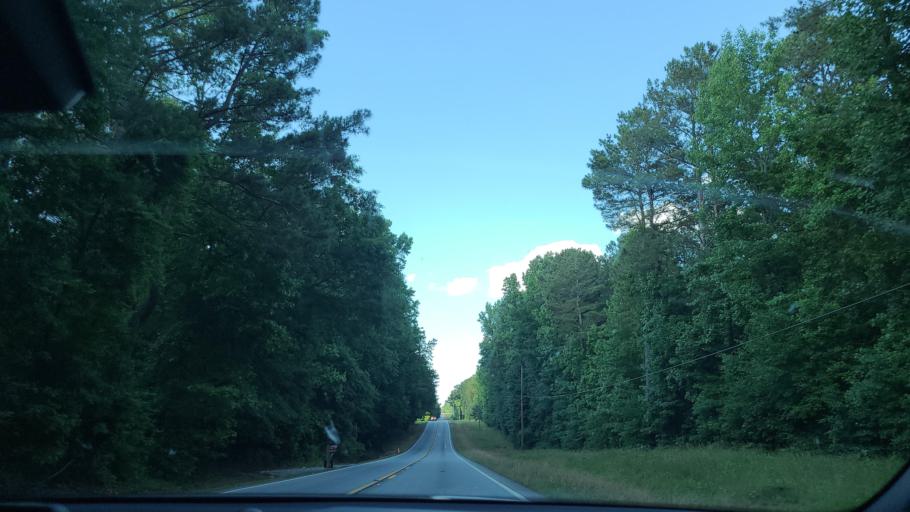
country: US
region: Georgia
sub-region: Oconee County
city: Watkinsville
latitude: 33.8299
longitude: -83.4358
